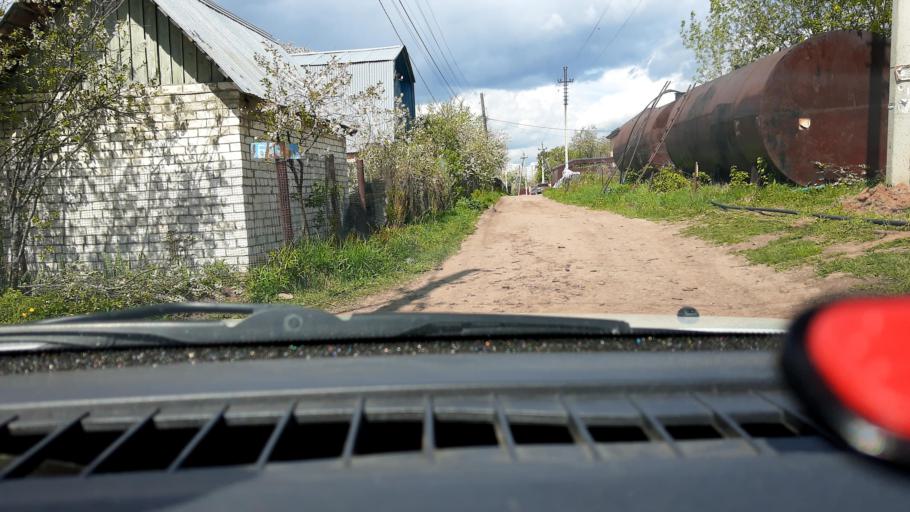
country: RU
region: Nizjnij Novgorod
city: Afonino
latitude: 56.2757
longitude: 44.0782
